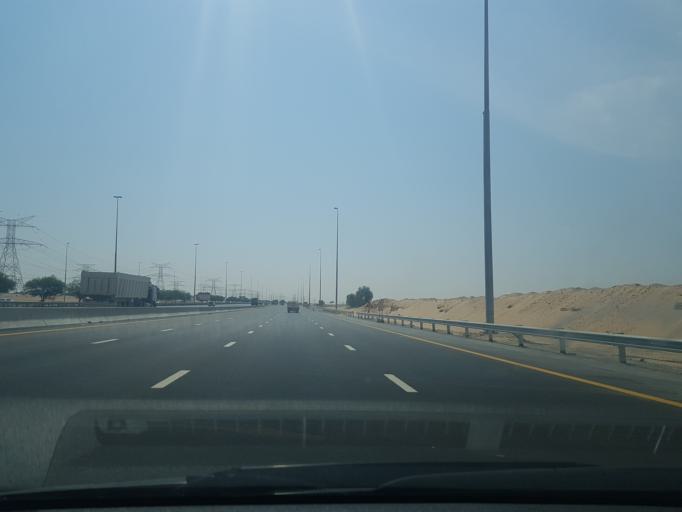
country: AE
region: Ash Shariqah
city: Sharjah
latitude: 25.2315
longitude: 55.5627
